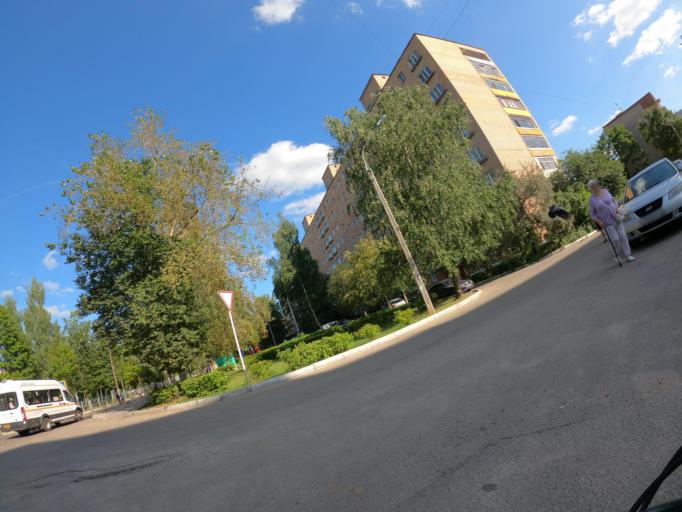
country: RU
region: Moskovskaya
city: Stupino
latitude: 54.8844
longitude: 38.0628
